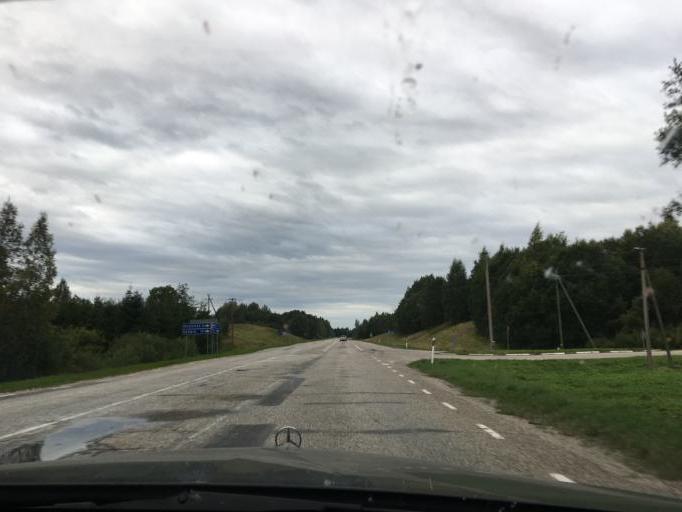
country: LV
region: Aluksnes Rajons
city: Aluksne
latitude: 57.5929
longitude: 27.0875
